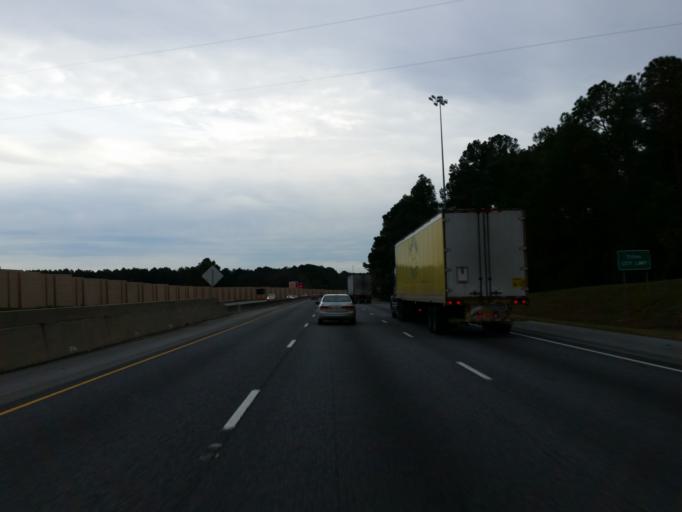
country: US
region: Georgia
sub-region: Tift County
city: Tifton
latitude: 31.4882
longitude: -83.5158
